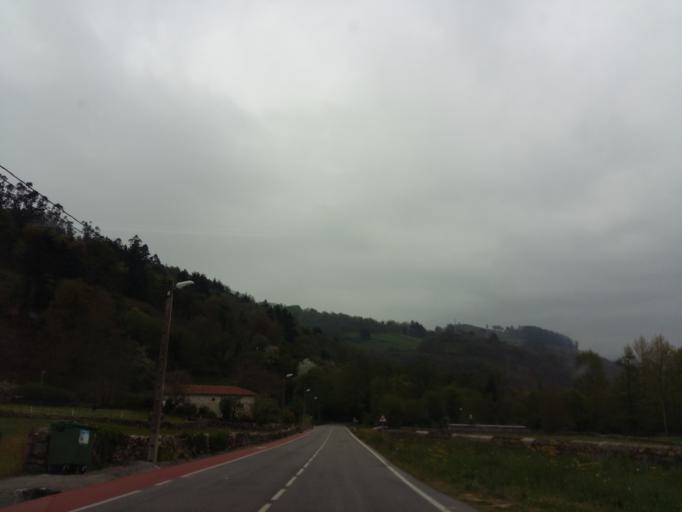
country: ES
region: Cantabria
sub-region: Provincia de Cantabria
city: Arenas de Iguna
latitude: 43.1952
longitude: -4.0607
